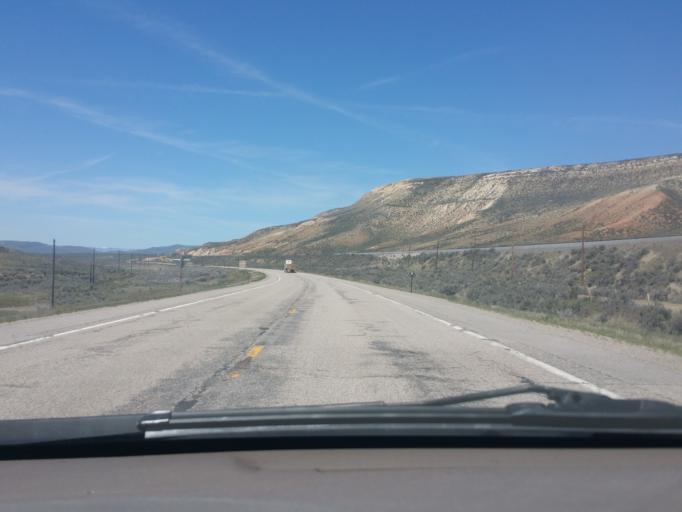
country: US
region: Wyoming
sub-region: Lincoln County
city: Kemmerer
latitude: 41.8152
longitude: -110.6304
